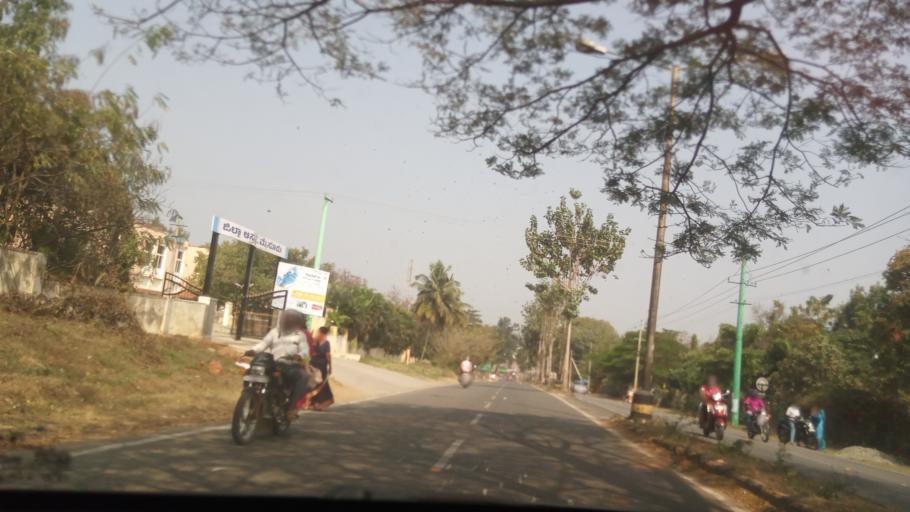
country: IN
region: Karnataka
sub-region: Mysore
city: Mysore
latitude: 12.3489
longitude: 76.6296
